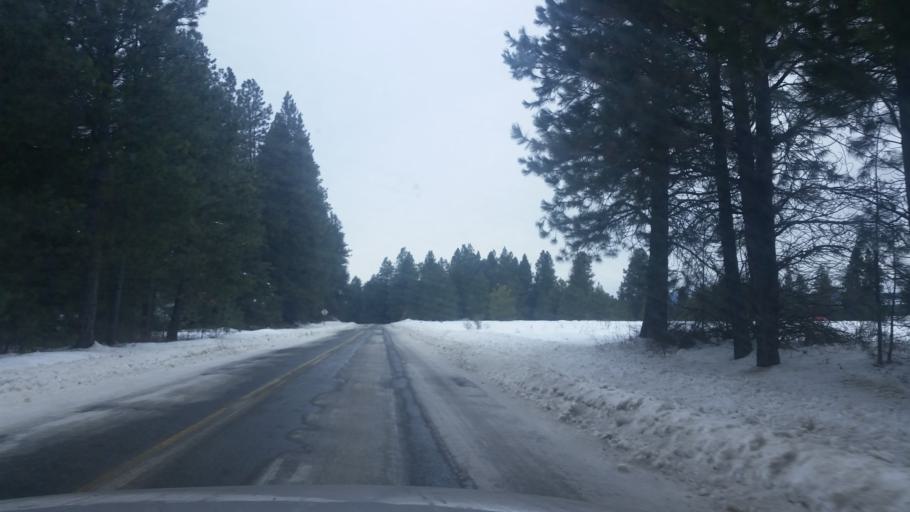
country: US
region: Washington
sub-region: Kittitas County
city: Cle Elum
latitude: 47.1576
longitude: -120.8371
